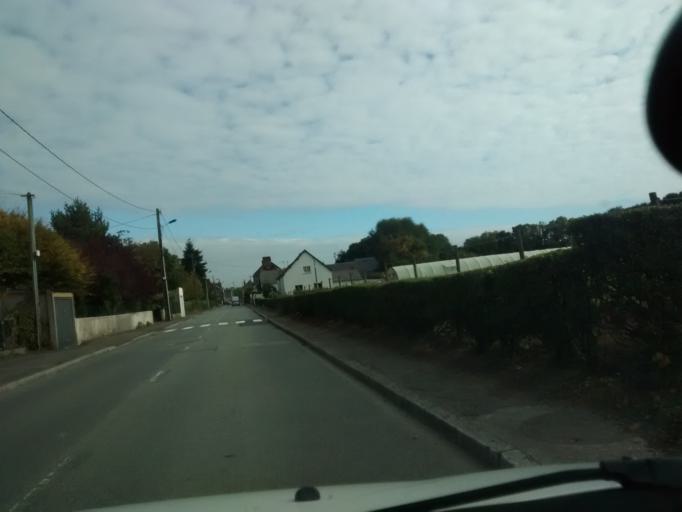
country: FR
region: Brittany
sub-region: Departement d'Ille-et-Vilaine
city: Saint-Jacques-de-la-Lande
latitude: 48.0994
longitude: -1.7238
